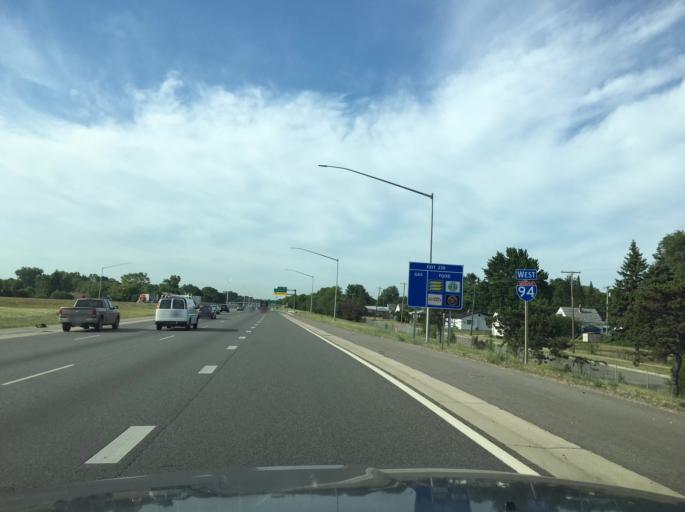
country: US
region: Michigan
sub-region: Macomb County
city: Roseville
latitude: 42.5184
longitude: -82.9189
